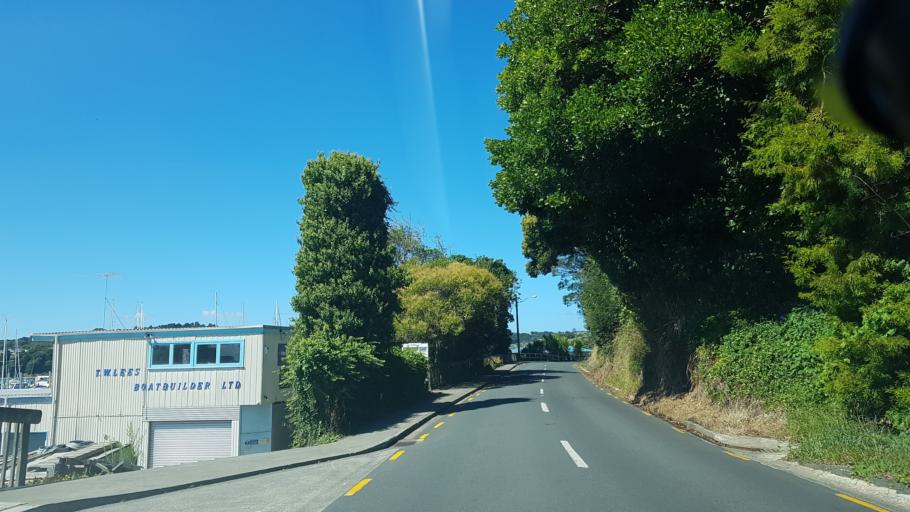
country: NZ
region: Auckland
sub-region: Auckland
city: Warkworth
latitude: -36.3920
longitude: 174.7240
